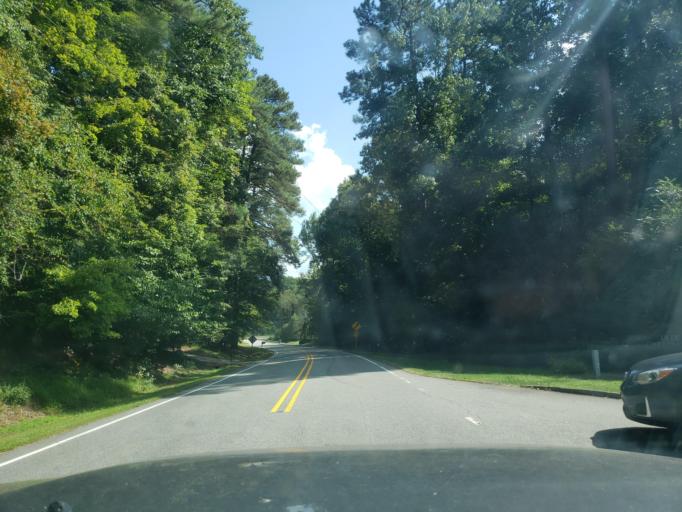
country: US
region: North Carolina
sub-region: Wake County
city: West Raleigh
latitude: 35.9282
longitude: -78.6895
